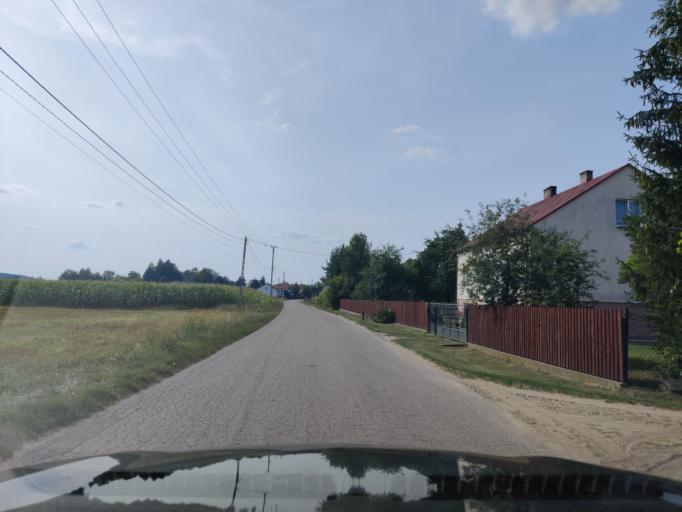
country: PL
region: Masovian Voivodeship
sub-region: Powiat wyszkowski
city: Rzasnik
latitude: 52.7394
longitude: 21.3373
